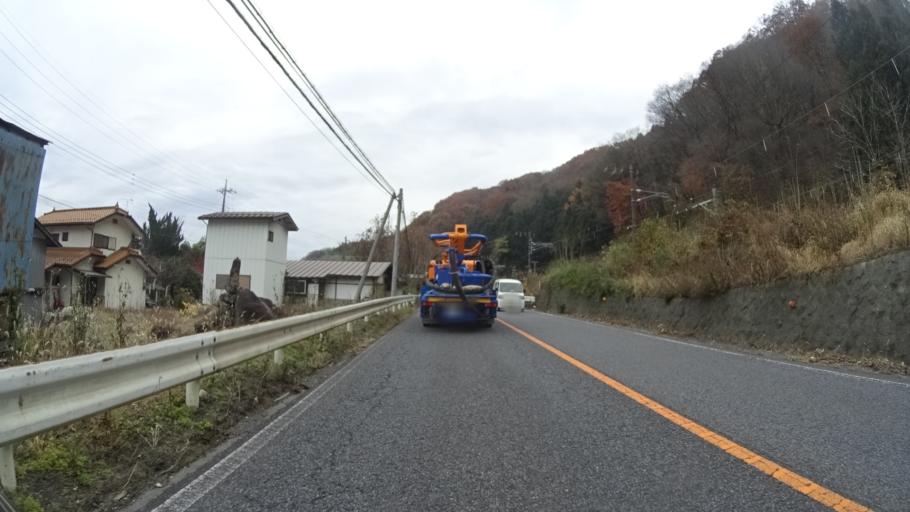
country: JP
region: Gunma
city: Numata
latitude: 36.6111
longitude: 139.0416
